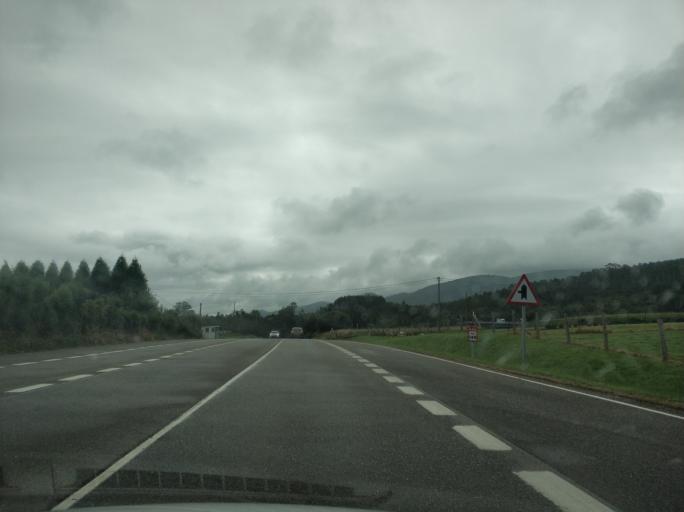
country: ES
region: Asturias
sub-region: Province of Asturias
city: Salas
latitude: 43.5427
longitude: -6.4114
